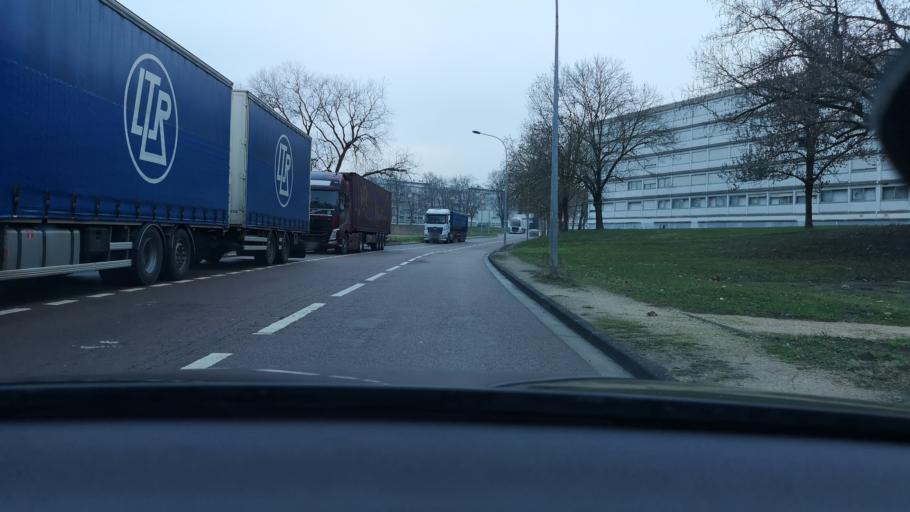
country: FR
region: Bourgogne
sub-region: Departement de Saone-et-Loire
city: Champforgeuil
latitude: 46.8037
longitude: 4.8420
